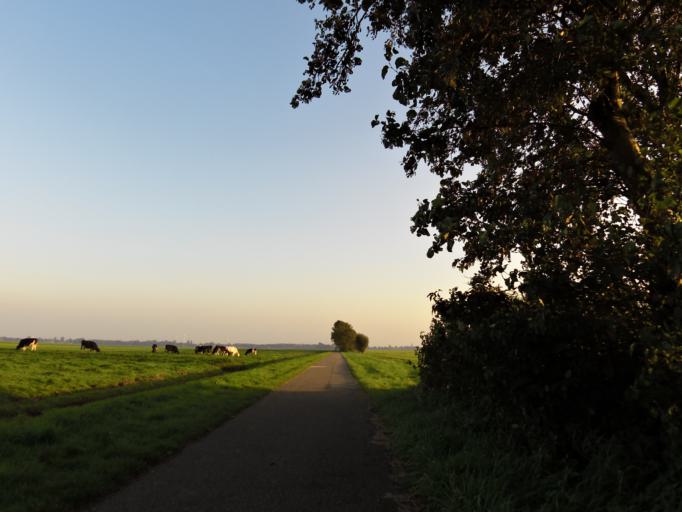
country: NL
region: South Holland
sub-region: Gemeente Leiderdorp
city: Leiderdorp
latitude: 52.1504
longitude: 4.5830
